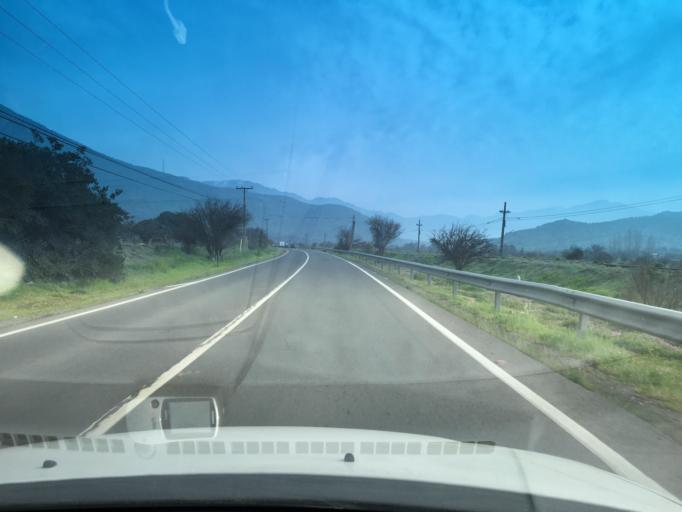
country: CL
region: Santiago Metropolitan
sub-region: Provincia de Chacabuco
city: Lampa
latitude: -33.1538
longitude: -70.9027
